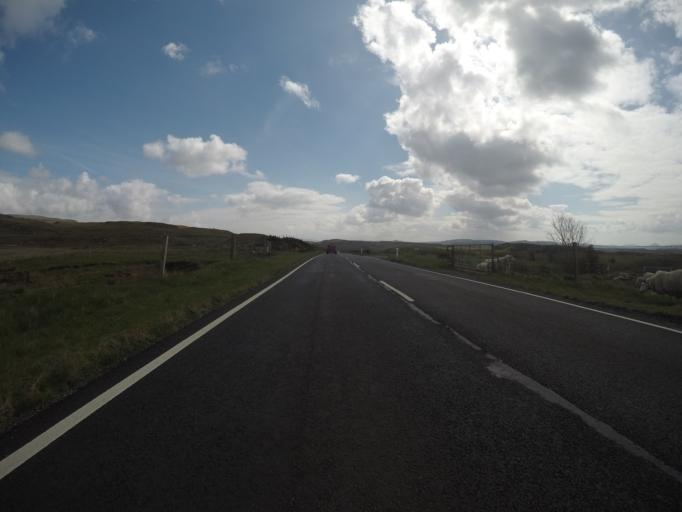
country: GB
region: Scotland
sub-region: Highland
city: Portree
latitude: 57.5389
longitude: -6.3627
